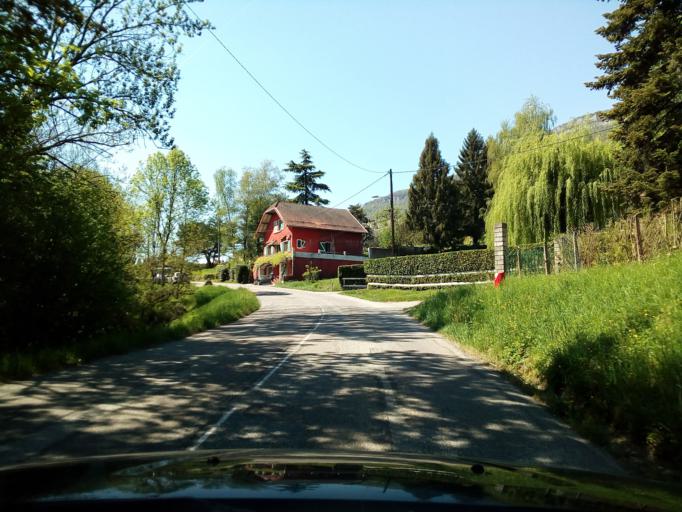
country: FR
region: Rhone-Alpes
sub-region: Departement de l'Isere
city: Barraux
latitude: 45.4307
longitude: 5.9873
